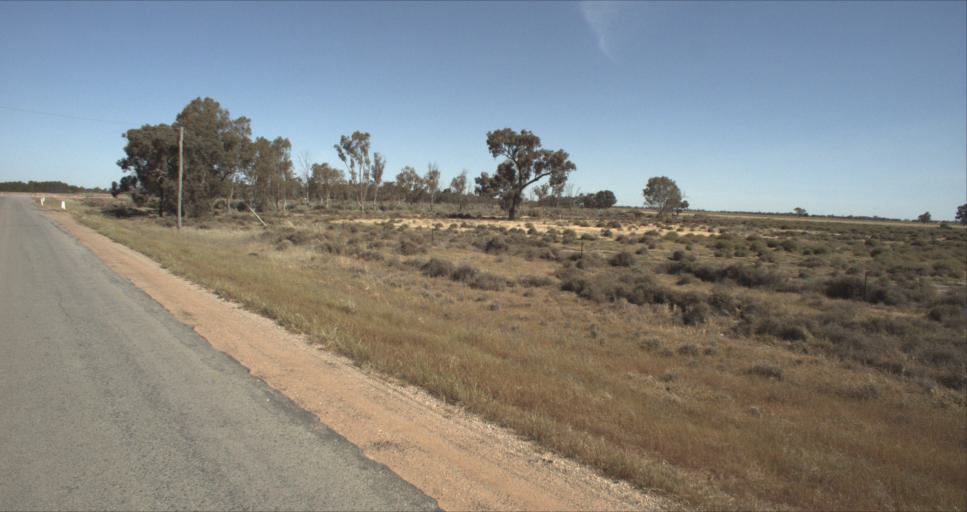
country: AU
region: New South Wales
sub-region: Leeton
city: Leeton
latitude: -34.4987
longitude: 146.3925
